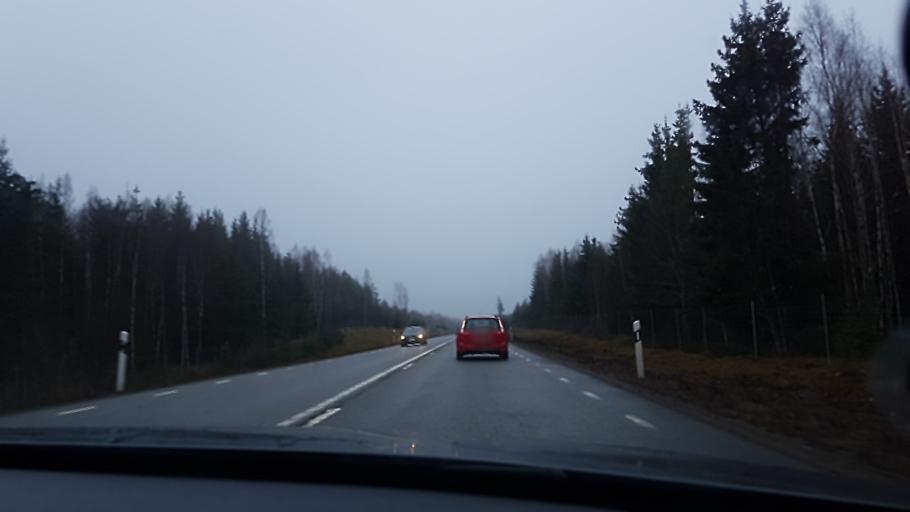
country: SE
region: Vaestra Goetaland
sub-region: Gullspangs Kommun
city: Gullspang
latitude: 58.8685
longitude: 14.0085
